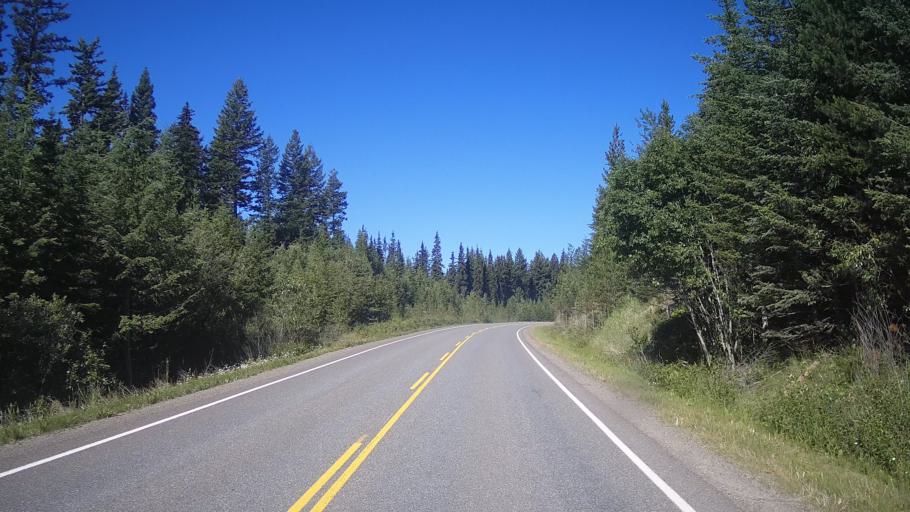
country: CA
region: British Columbia
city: Kamloops
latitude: 51.4969
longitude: -120.4279
